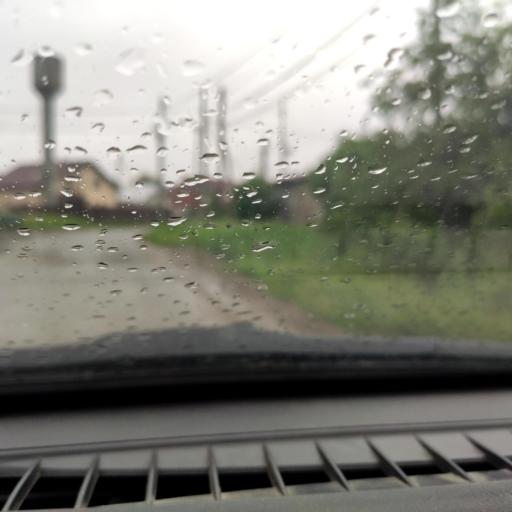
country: RU
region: Samara
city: Tol'yatti
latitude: 53.5655
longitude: 49.3810
